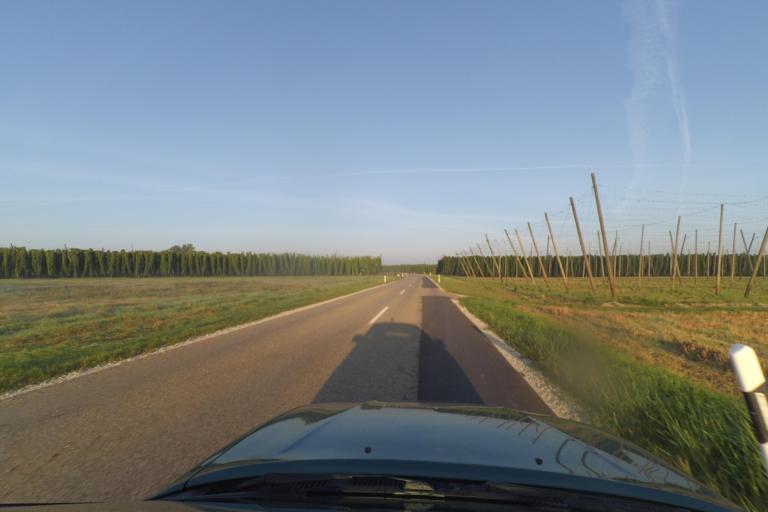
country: DE
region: Bavaria
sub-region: Upper Bavaria
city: Geisenfeld
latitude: 48.6807
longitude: 11.6522
